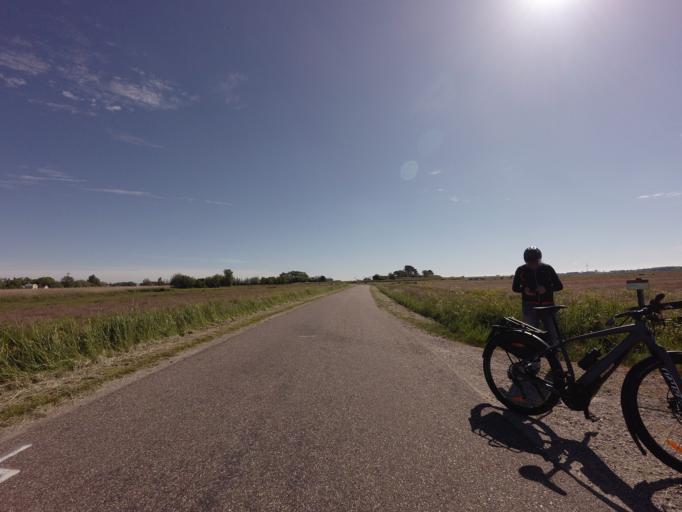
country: NL
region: North Holland
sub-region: Gemeente Uitgeest
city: Uitgeest
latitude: 52.5200
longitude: 4.7462
